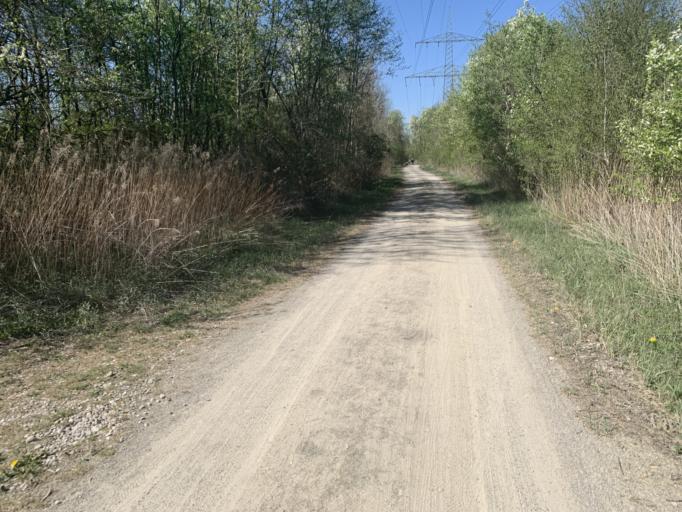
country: DE
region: Bavaria
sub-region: Swabia
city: Gersthofen
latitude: 48.4540
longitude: 10.8867
